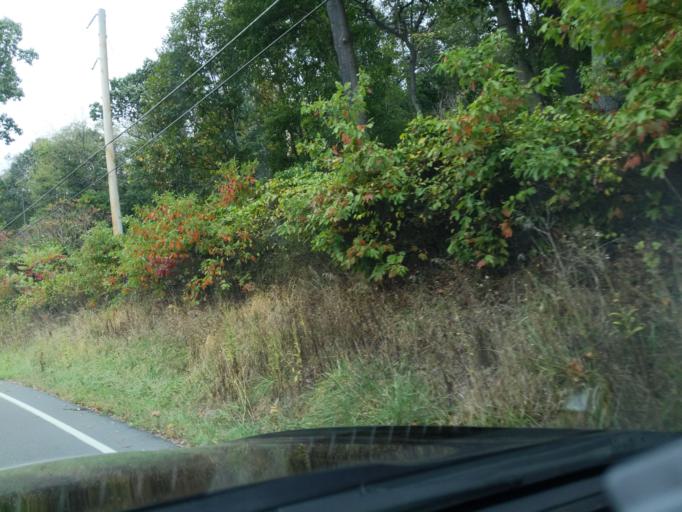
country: US
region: Pennsylvania
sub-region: Blair County
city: Altoona
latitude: 40.4895
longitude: -78.4367
